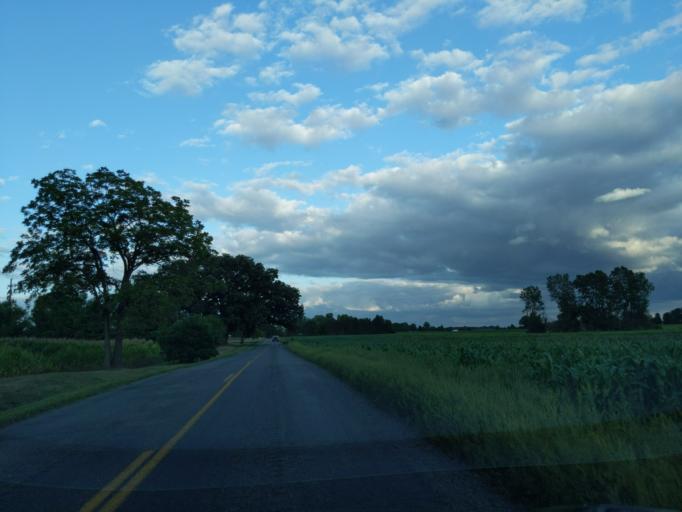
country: US
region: Michigan
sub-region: Ingham County
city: Holt
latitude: 42.5968
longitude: -84.5573
